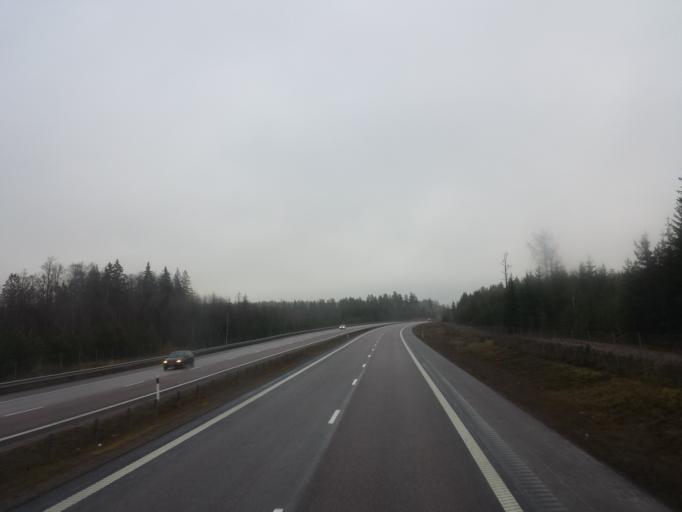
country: SE
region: Soedermanland
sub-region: Nykopings Kommun
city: Olstorp
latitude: 58.7501
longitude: 16.5270
